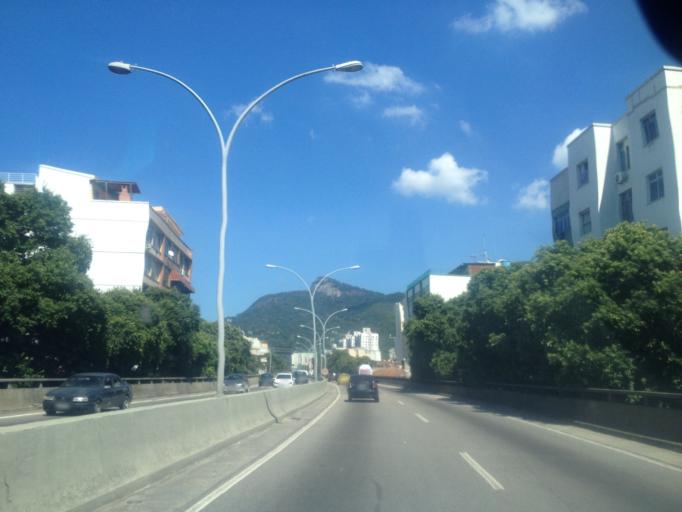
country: BR
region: Rio de Janeiro
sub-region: Rio De Janeiro
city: Rio de Janeiro
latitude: -22.9145
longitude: -43.2101
